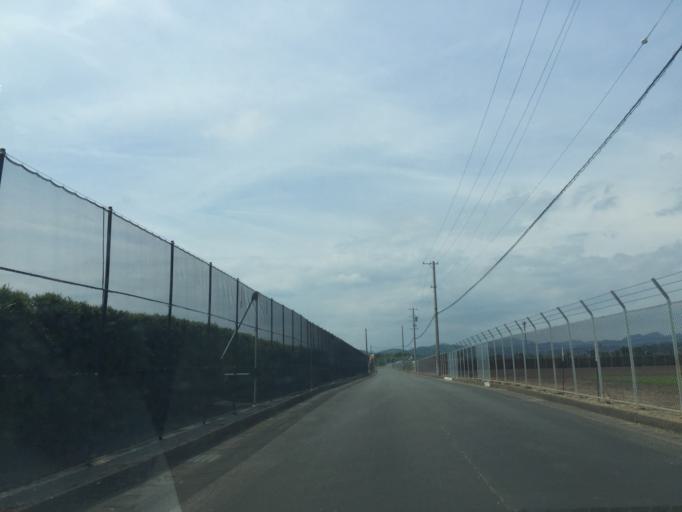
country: JP
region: Shizuoka
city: Mori
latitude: 34.7965
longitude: 137.9445
